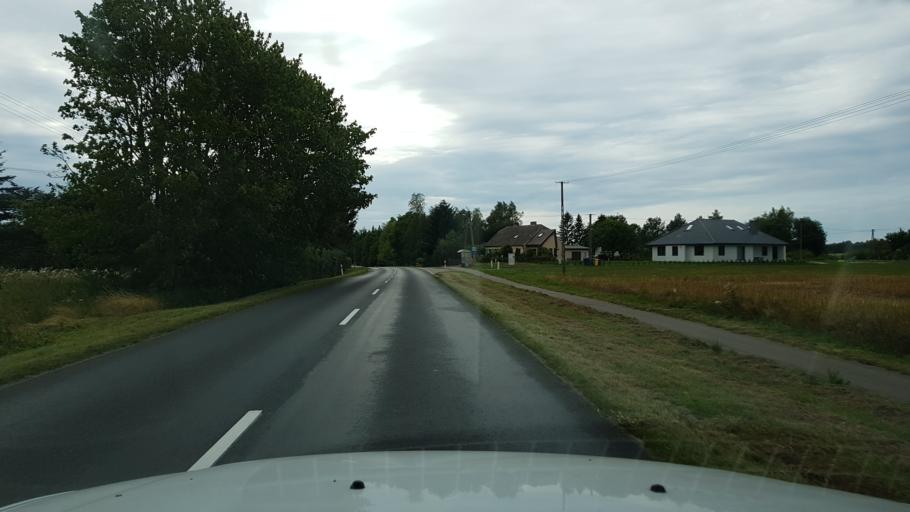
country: PL
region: West Pomeranian Voivodeship
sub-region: Powiat kolobrzeski
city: Dygowo
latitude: 54.1384
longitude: 15.7054
